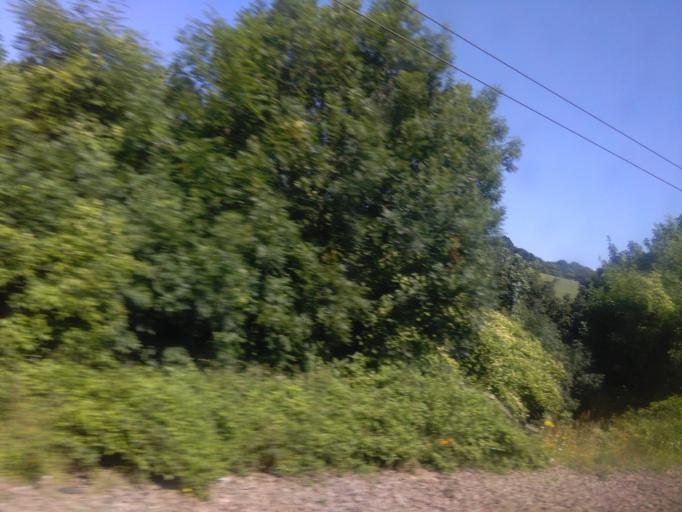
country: GB
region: England
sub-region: Hertfordshire
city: Harpenden
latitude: 51.8571
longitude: -0.3780
